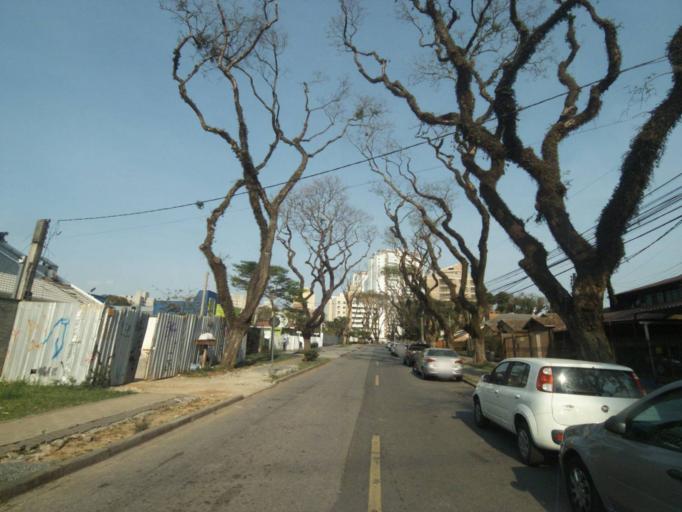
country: BR
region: Parana
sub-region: Curitiba
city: Curitiba
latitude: -25.4671
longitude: -49.2978
